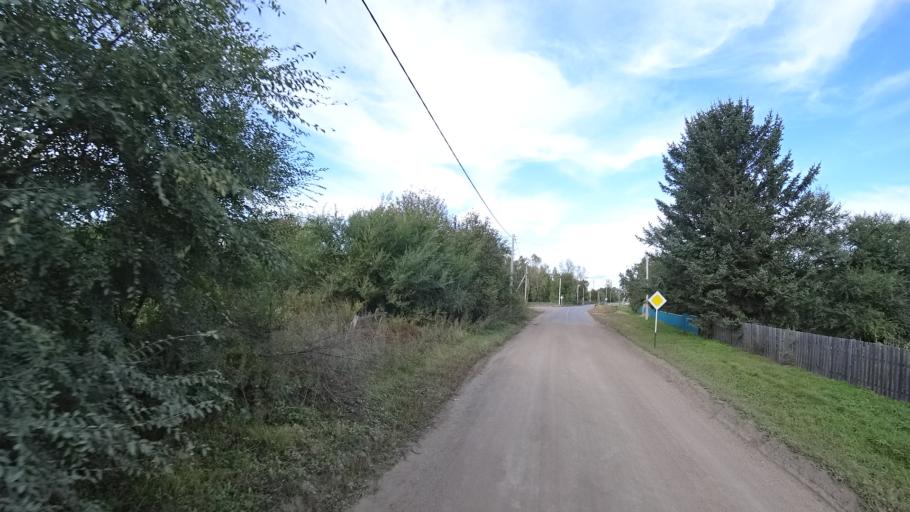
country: RU
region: Amur
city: Arkhara
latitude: 49.3589
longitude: 130.1167
